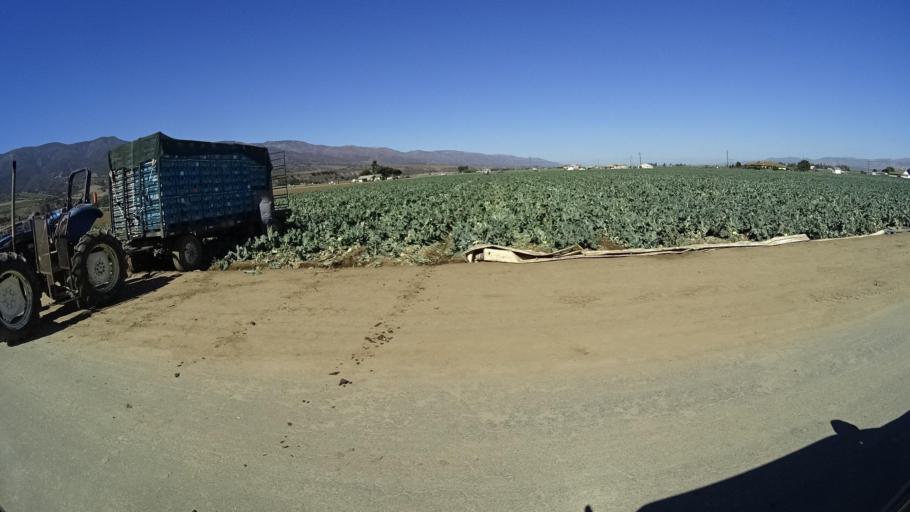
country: US
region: California
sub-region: Monterey County
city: Soledad
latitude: 36.3938
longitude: -121.3493
